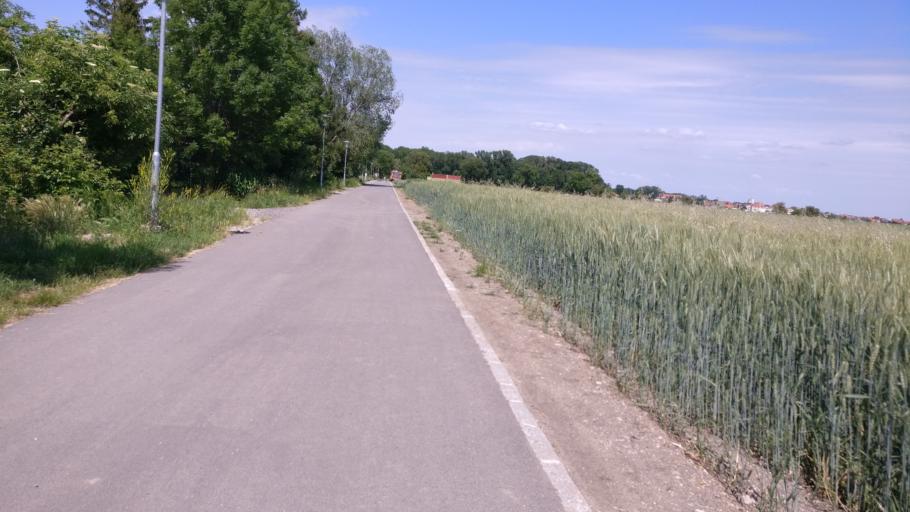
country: AT
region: Lower Austria
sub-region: Politischer Bezirk Baden
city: Gunselsdorf
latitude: 47.9429
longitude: 16.2635
